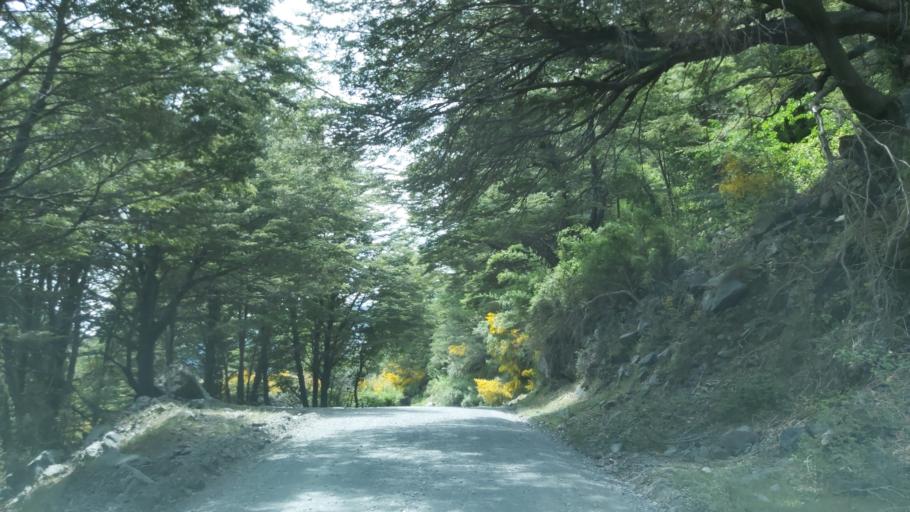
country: AR
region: Neuquen
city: Las Ovejas
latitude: -37.3971
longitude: -71.4488
